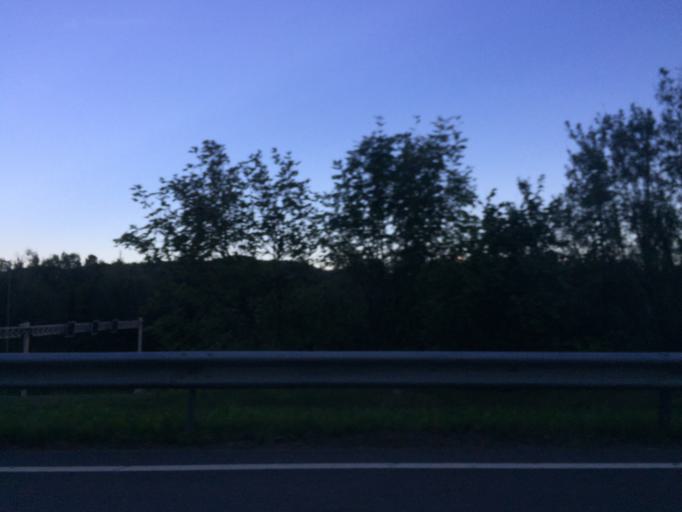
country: NO
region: Akershus
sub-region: Skedsmo
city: Lillestrom
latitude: 59.9401
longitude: 11.0128
